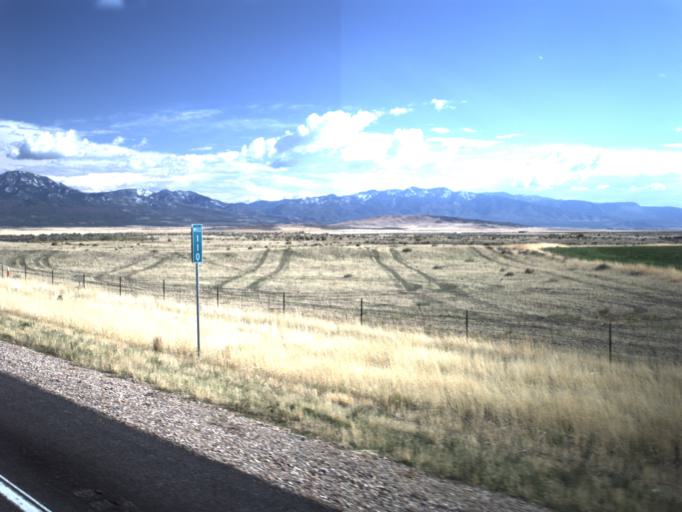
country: US
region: Utah
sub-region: Millard County
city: Fillmore
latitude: 39.1393
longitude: -112.3721
